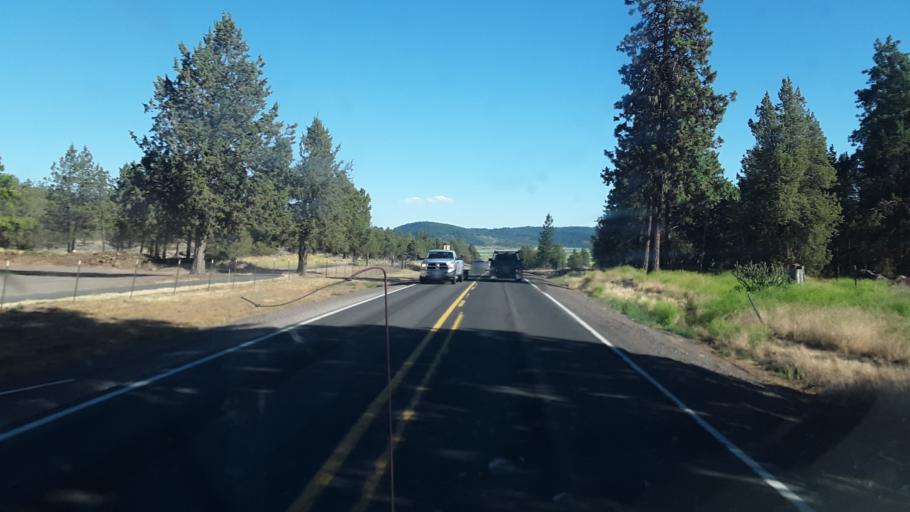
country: US
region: Oregon
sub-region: Klamath County
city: Klamath Falls
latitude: 42.2669
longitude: -121.8788
